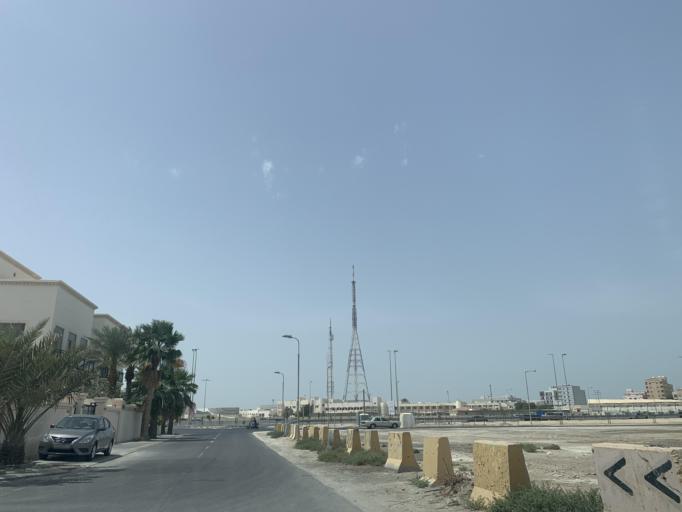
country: BH
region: Northern
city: Madinat `Isa
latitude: 26.1585
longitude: 50.5596
